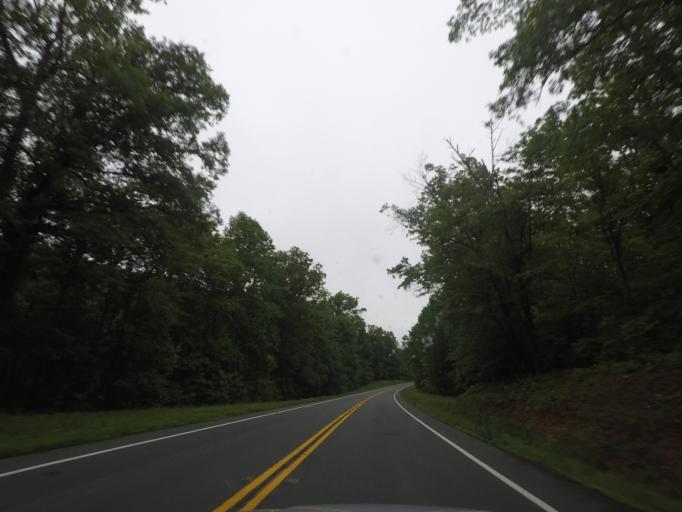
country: US
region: Virginia
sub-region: Fluvanna County
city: Weber City
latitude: 37.7306
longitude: -78.2972
